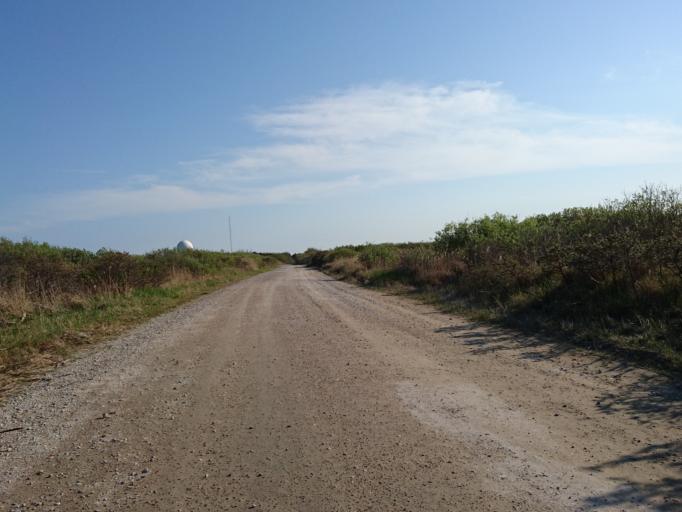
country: DK
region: North Denmark
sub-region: Frederikshavn Kommune
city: Skagen
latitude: 57.7498
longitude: 10.6039
